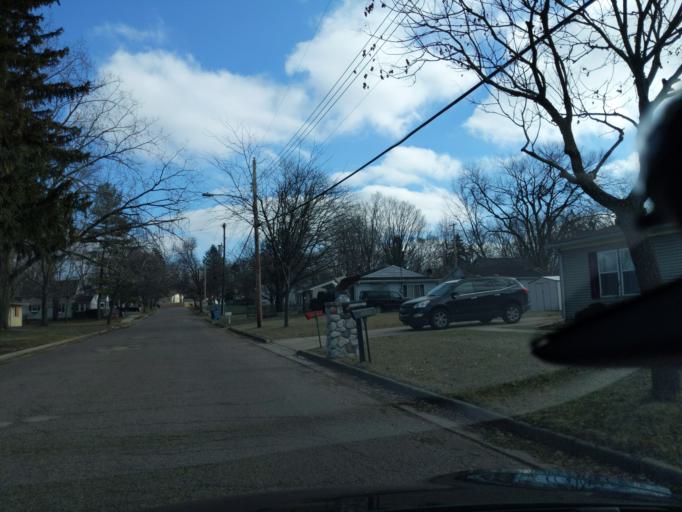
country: US
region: Michigan
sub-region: Ingham County
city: Lansing
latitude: 42.6730
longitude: -84.5836
